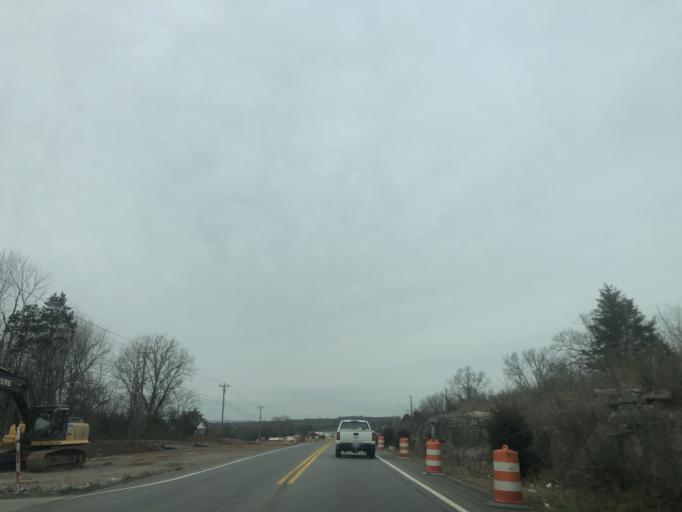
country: US
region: Tennessee
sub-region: Wilson County
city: Mount Juliet
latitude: 36.2589
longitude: -86.4387
